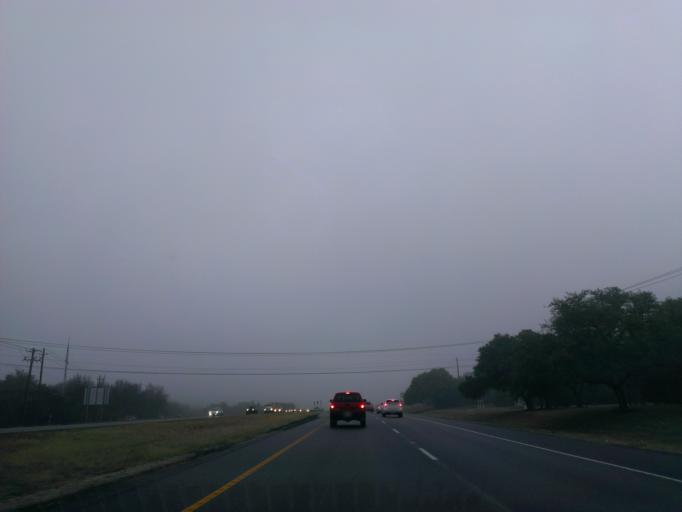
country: US
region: Texas
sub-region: Williamson County
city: Jollyville
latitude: 30.3750
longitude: -97.7815
